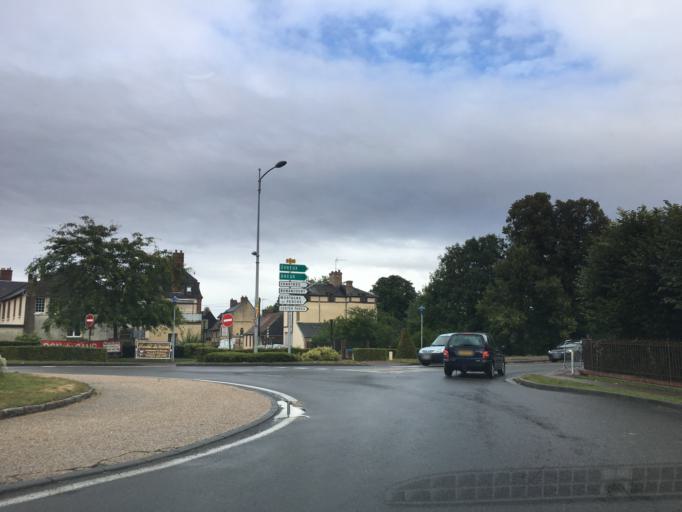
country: FR
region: Haute-Normandie
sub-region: Departement de l'Eure
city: Verneuil-sur-Avre
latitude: 48.7381
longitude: 0.9200
